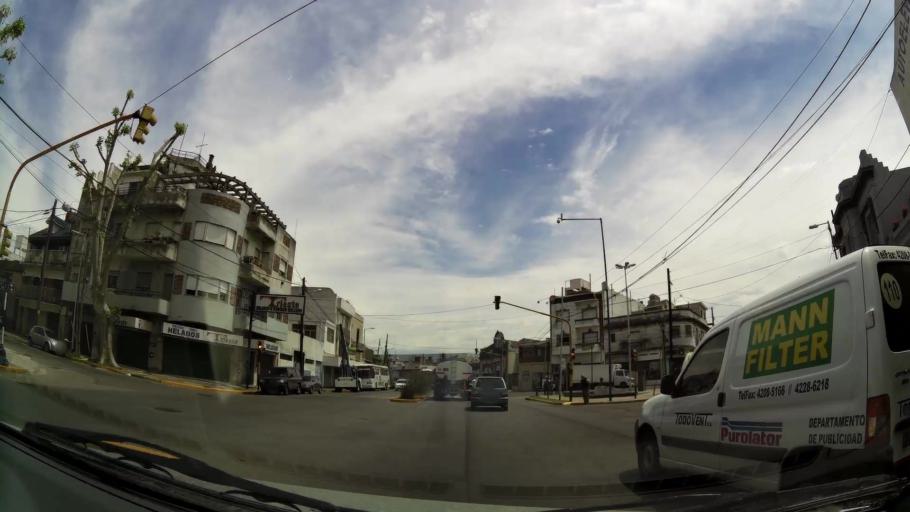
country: AR
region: Buenos Aires
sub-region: Partido de Avellaneda
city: Avellaneda
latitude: -34.6672
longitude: -58.3838
